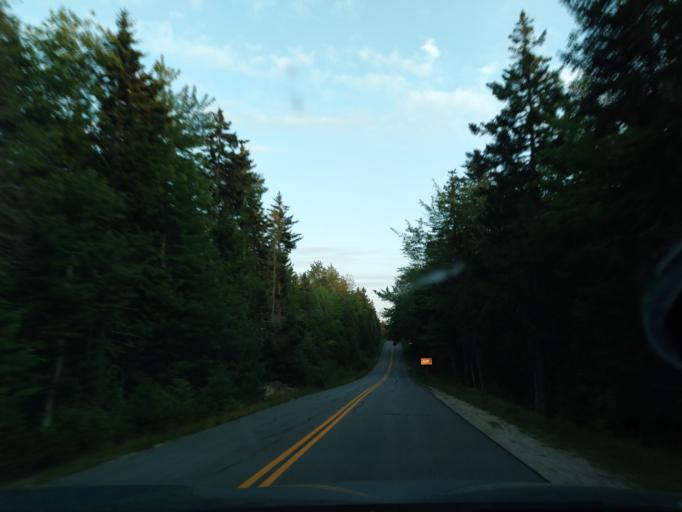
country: US
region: Maine
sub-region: Hancock County
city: Gouldsboro
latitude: 44.3839
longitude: -68.0693
